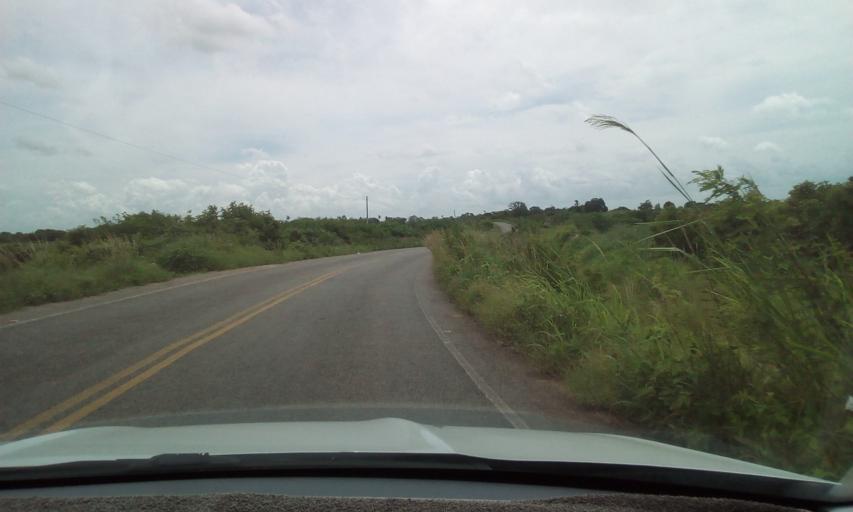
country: BR
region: Paraiba
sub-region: Mari
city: Mari
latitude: -7.1223
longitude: -35.3482
